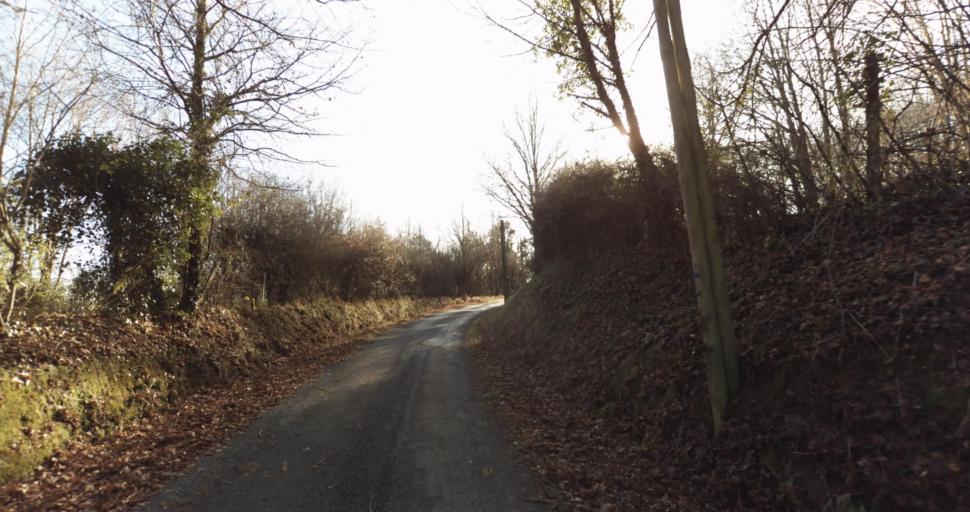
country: FR
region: Limousin
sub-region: Departement de la Haute-Vienne
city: Aixe-sur-Vienne
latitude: 45.7795
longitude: 1.1288
